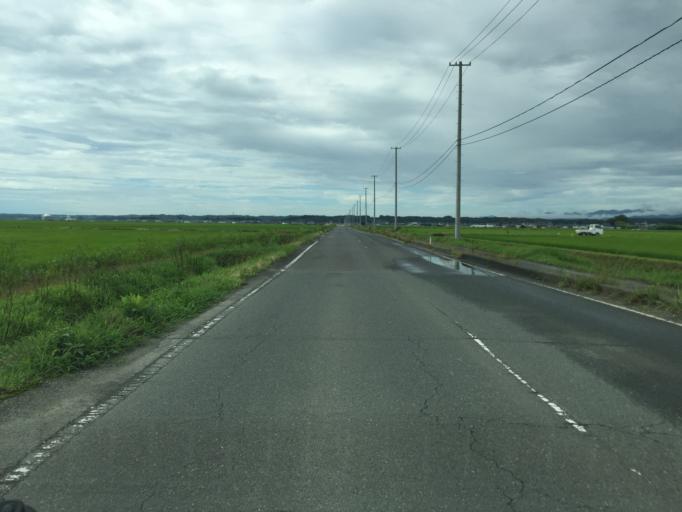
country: JP
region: Miyagi
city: Marumori
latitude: 37.8024
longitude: 140.9566
